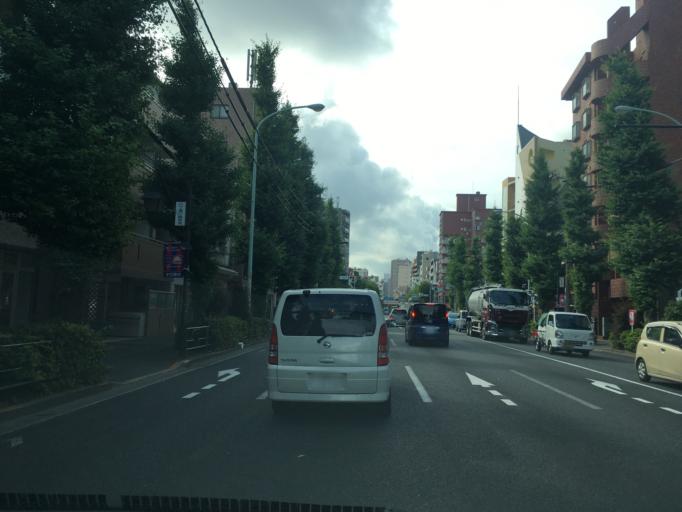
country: JP
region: Tokyo
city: Musashino
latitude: 35.7087
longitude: 139.6141
